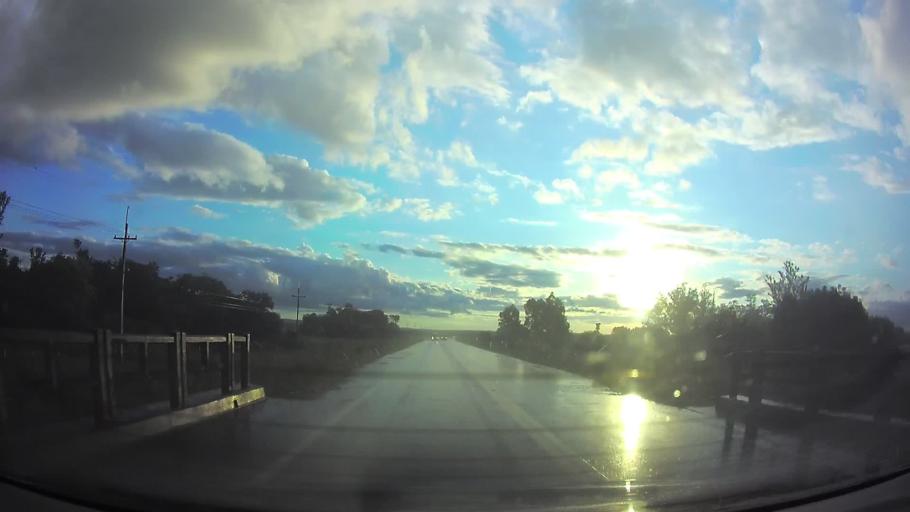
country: PY
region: Paraguari
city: Paraguari
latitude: -25.7085
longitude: -57.1869
